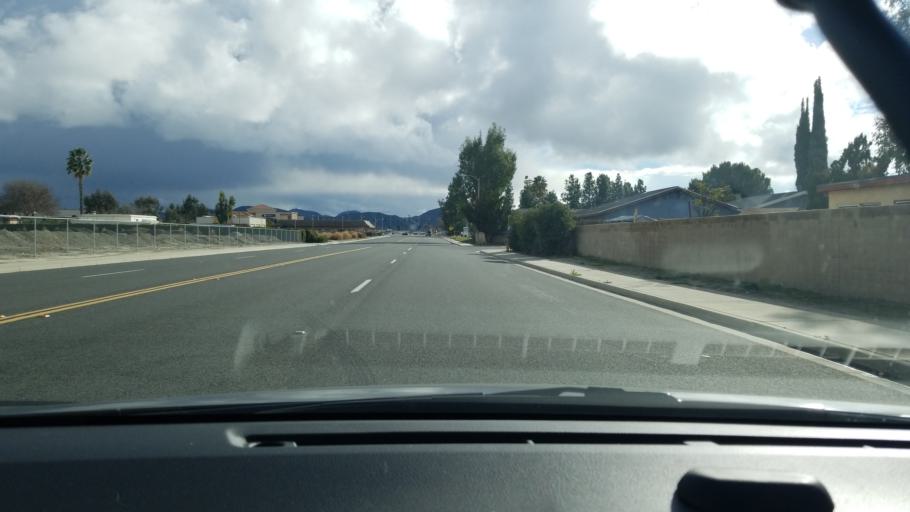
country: US
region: California
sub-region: Riverside County
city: Hemet
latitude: 33.7484
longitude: -117.0155
